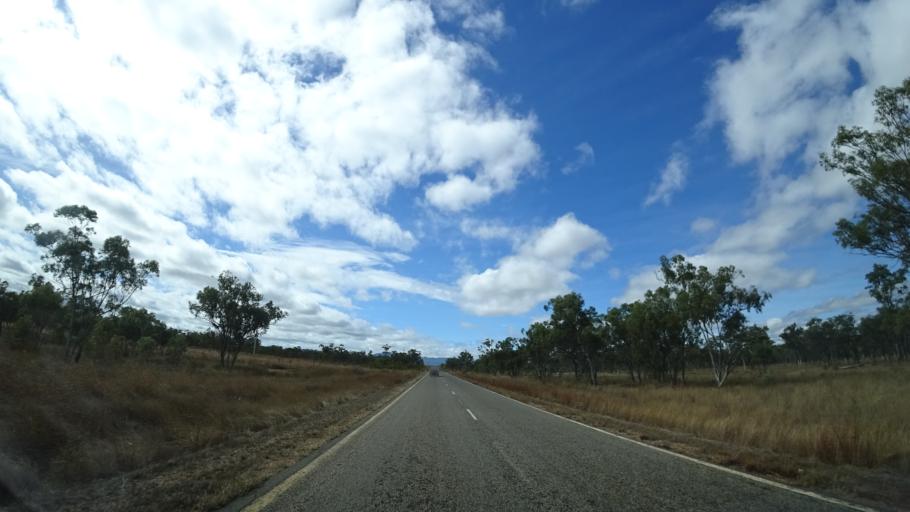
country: AU
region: Queensland
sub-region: Cairns
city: Port Douglas
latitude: -16.4972
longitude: 144.9841
